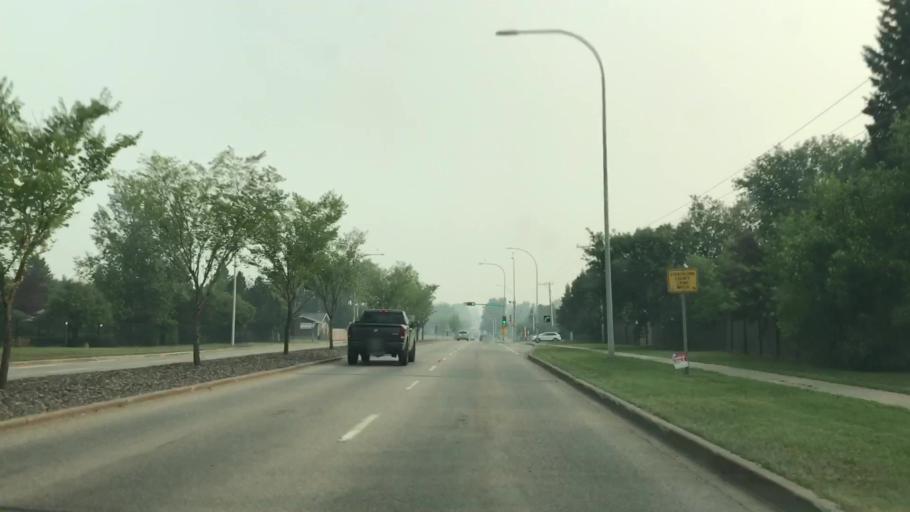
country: CA
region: Alberta
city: Sherwood Park
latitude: 53.5223
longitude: -113.3201
